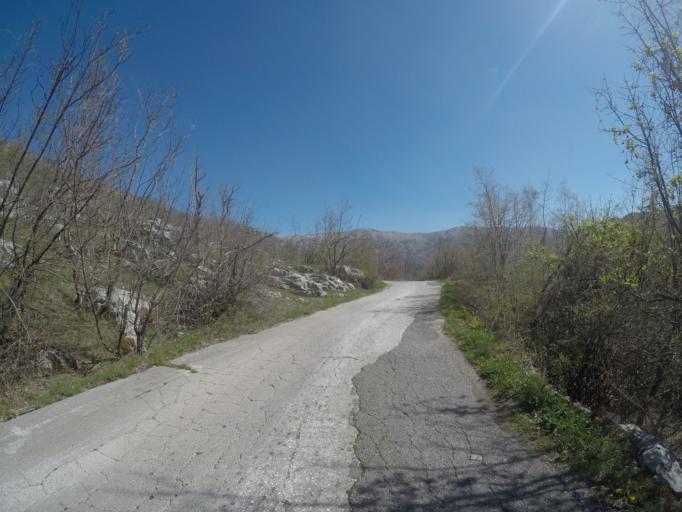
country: ME
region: Cetinje
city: Cetinje
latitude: 42.5357
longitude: 18.9796
